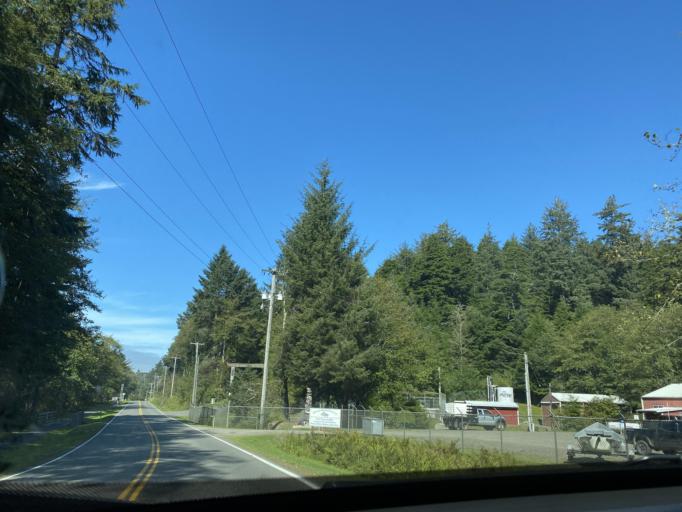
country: US
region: Washington
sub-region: Clallam County
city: Forks
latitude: 47.9018
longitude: -124.6272
